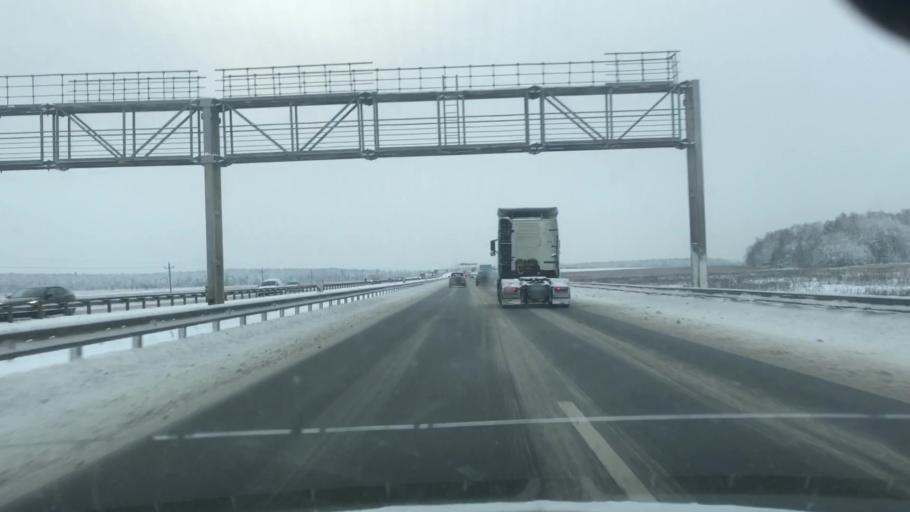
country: RU
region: Moskovskaya
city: Mikhnevo
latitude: 55.0880
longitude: 37.9324
